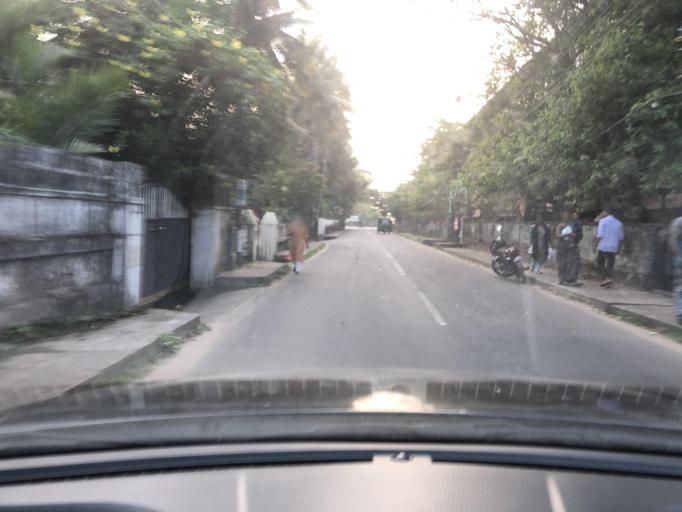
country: IN
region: Kerala
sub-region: Kozhikode
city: Kozhikode
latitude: 11.2913
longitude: 75.7599
